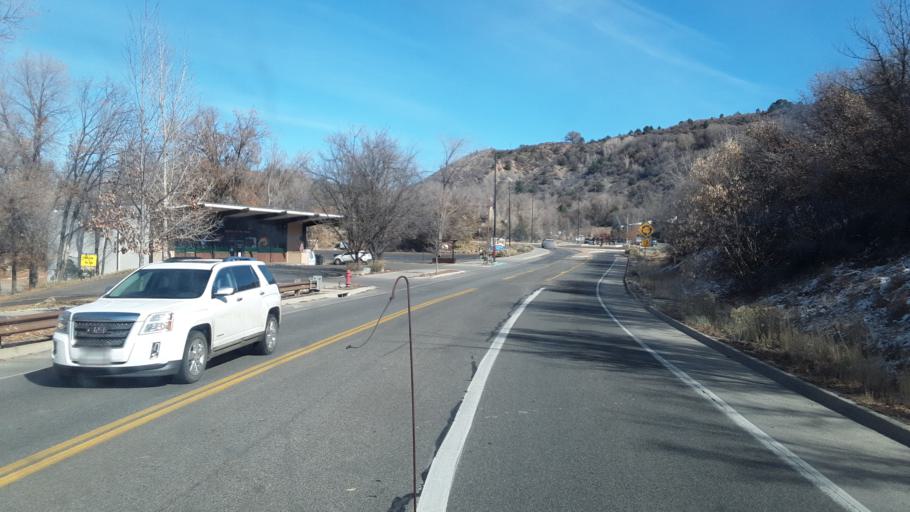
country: US
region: Colorado
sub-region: La Plata County
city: Durango
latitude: 37.2826
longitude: -107.8708
